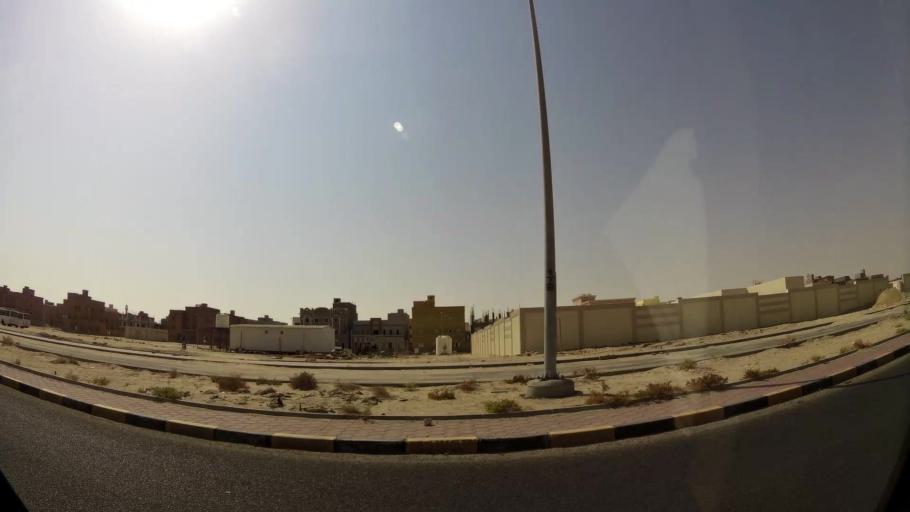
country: KW
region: Al Ahmadi
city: Al Wafrah
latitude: 28.8016
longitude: 48.0514
